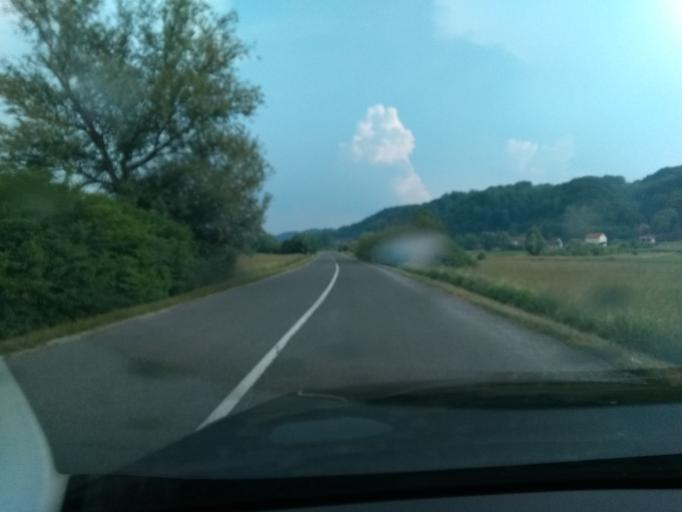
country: HR
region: Krapinsko-Zagorska
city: Pregrada
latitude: 46.0652
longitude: 15.7941
